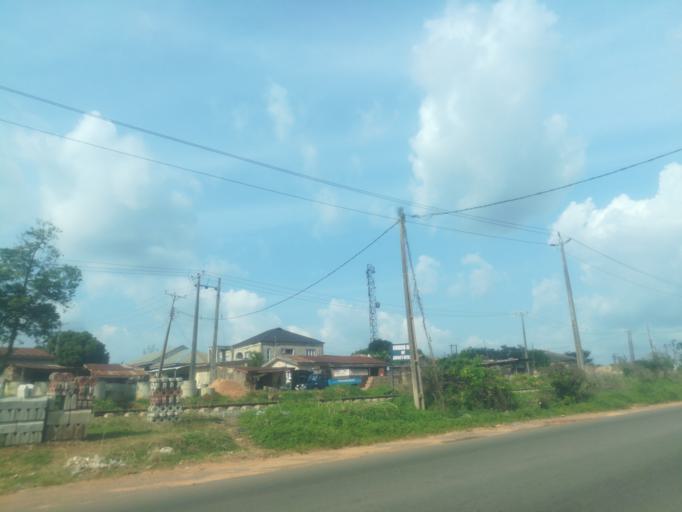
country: NG
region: Oyo
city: Ido
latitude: 7.3969
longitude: 3.7956
